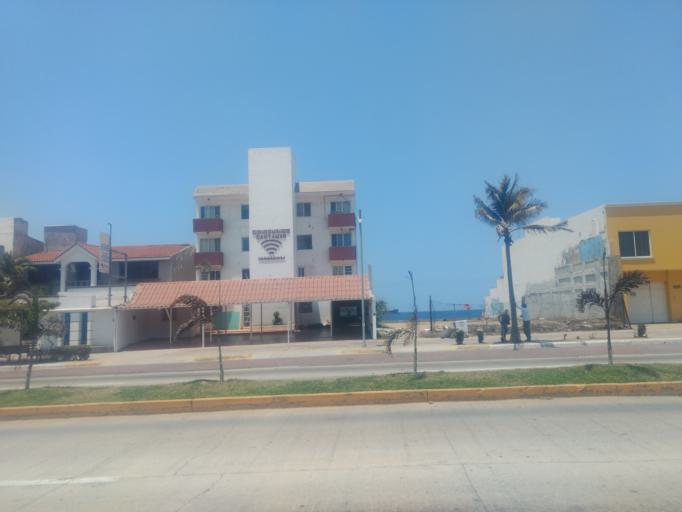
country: MX
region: Colima
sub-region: Manzanillo
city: Manzanillo
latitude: 19.0929
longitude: -104.3164
